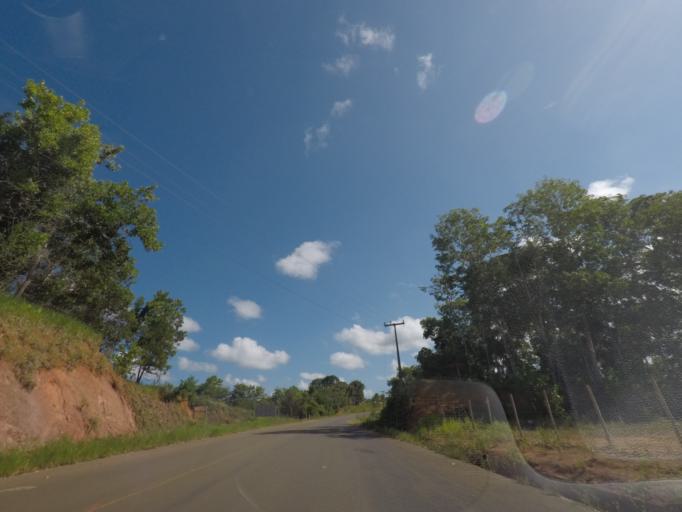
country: BR
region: Bahia
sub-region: Camamu
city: Camamu
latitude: -13.9541
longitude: -39.1069
